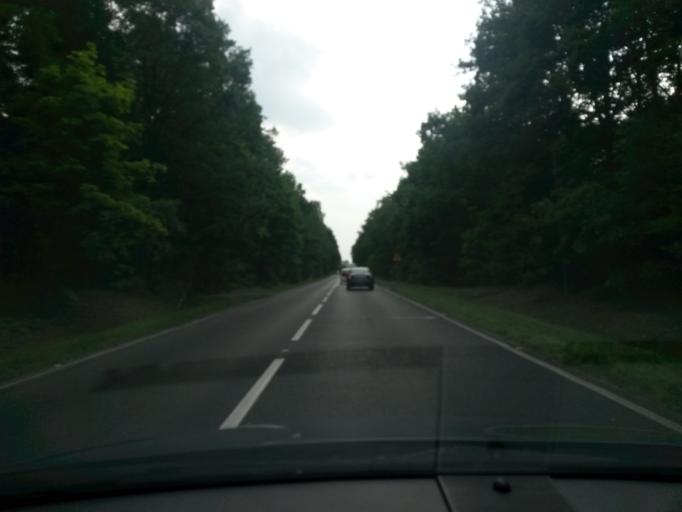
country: PL
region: Greater Poland Voivodeship
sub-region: Powiat poznanski
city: Kornik
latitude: 52.1941
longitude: 17.0607
